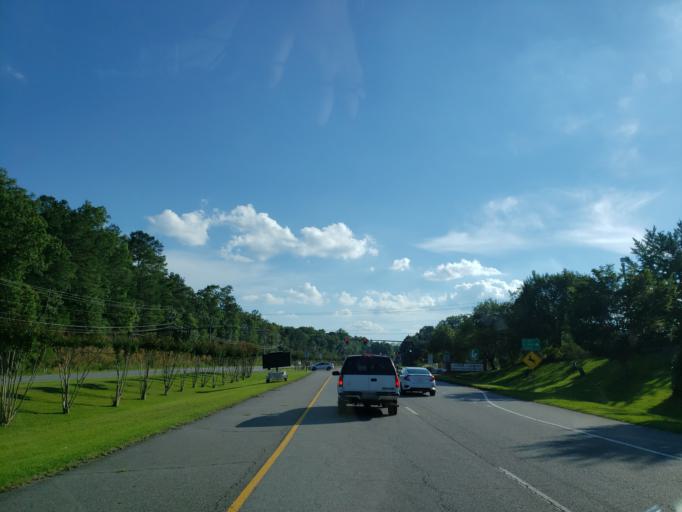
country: US
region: Georgia
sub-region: Cherokee County
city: Canton
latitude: 34.2373
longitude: -84.4682
